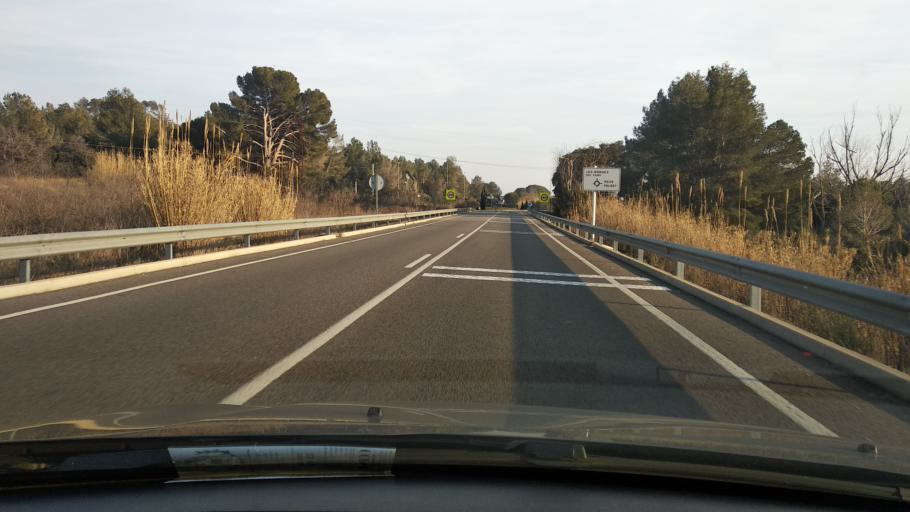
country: ES
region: Catalonia
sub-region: Provincia de Tarragona
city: les Borges del Camp
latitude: 41.1834
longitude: 1.0082
